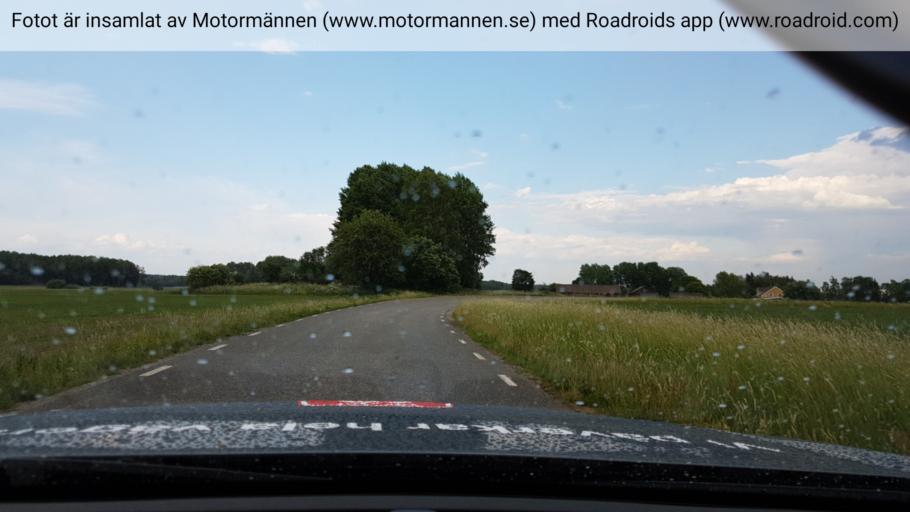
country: SE
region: Vaestmanland
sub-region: Vasteras
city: Skultuna
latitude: 59.7076
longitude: 16.4392
